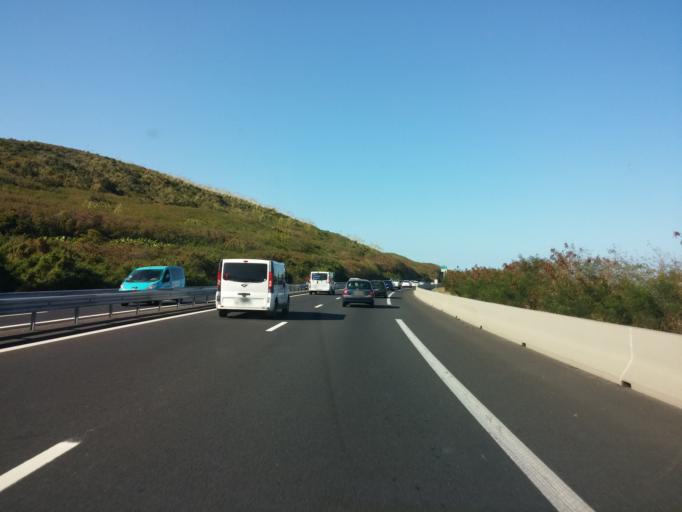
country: RE
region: Reunion
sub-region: Reunion
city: Saint-Leu
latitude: -21.1338
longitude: 55.2848
